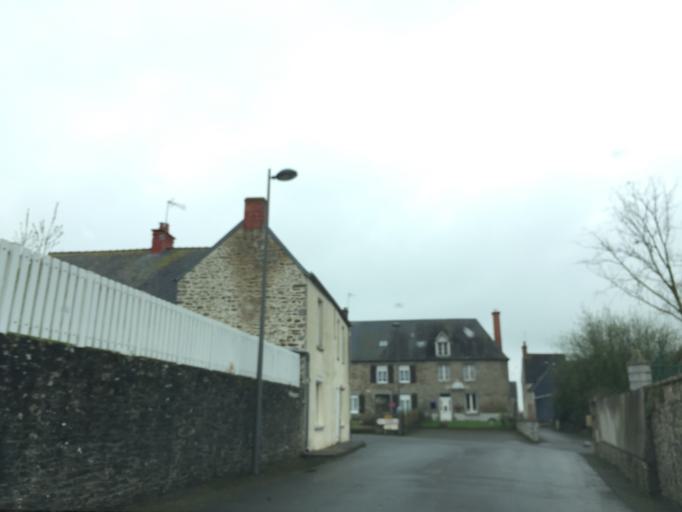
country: FR
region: Lower Normandy
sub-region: Departement de la Manche
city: Saint-James
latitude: 48.5618
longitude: -1.3998
